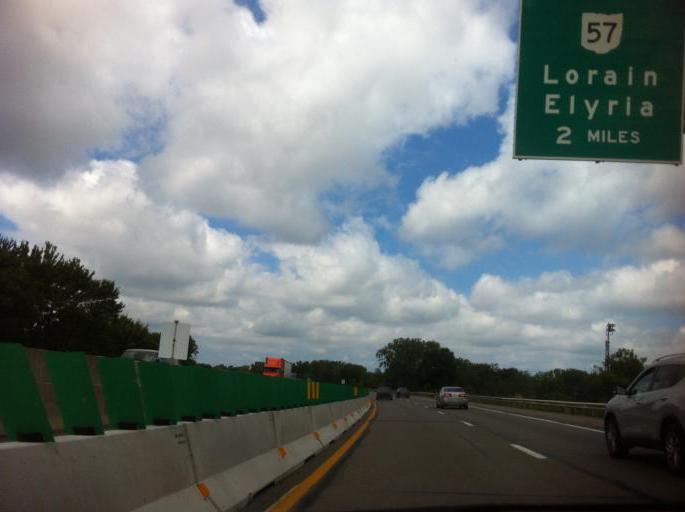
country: US
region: Ohio
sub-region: Lorain County
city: Elyria
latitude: 41.3841
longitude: -82.0713
